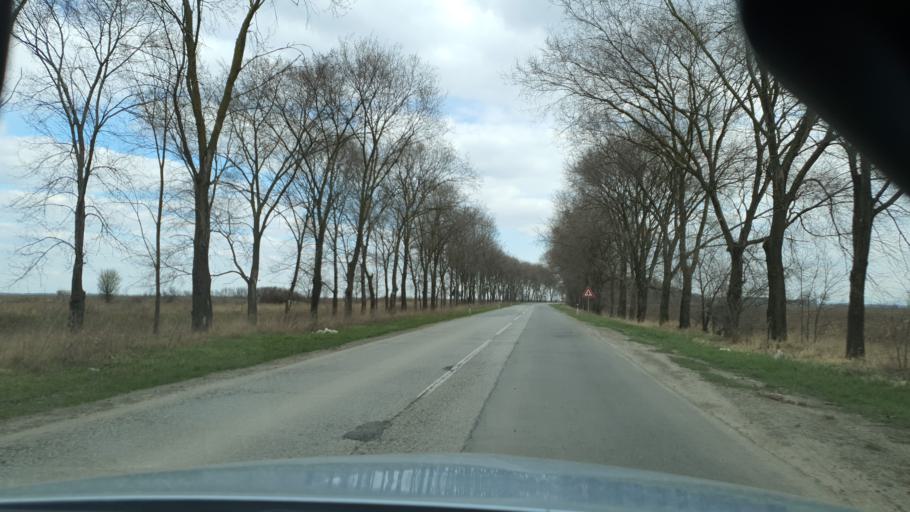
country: RS
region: Autonomna Pokrajina Vojvodina
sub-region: Zapadnobacki Okrug
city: Odzaci
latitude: 45.4484
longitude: 19.3557
